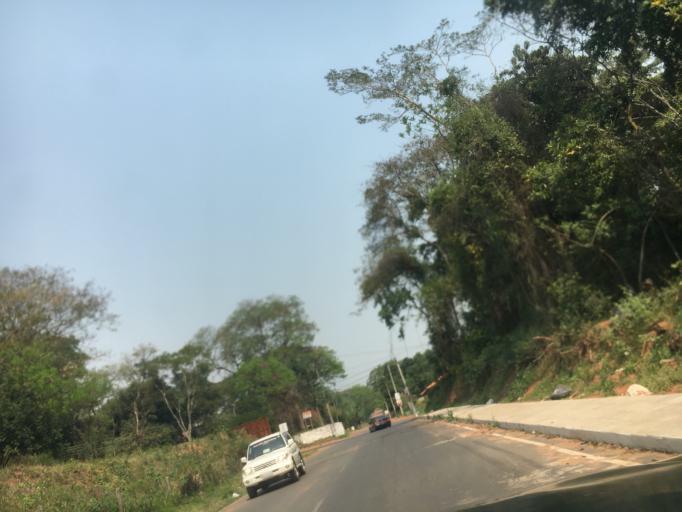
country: PY
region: Central
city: Villa Elisa
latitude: -25.3789
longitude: -57.5908
